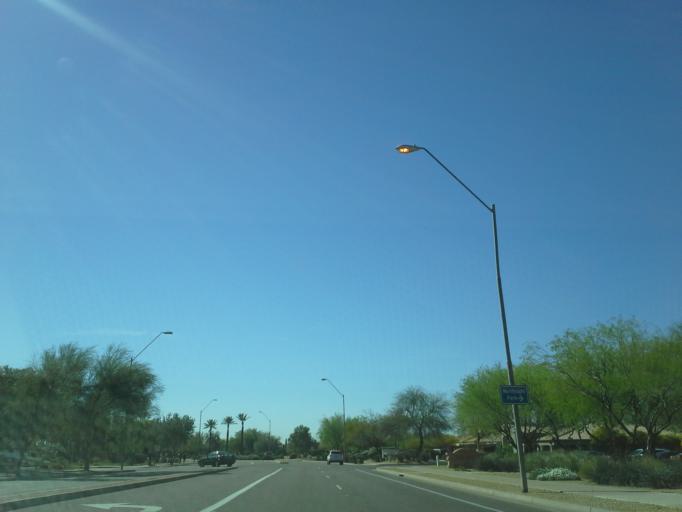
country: US
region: Arizona
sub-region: Maricopa County
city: Paradise Valley
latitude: 33.6154
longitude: -111.8978
